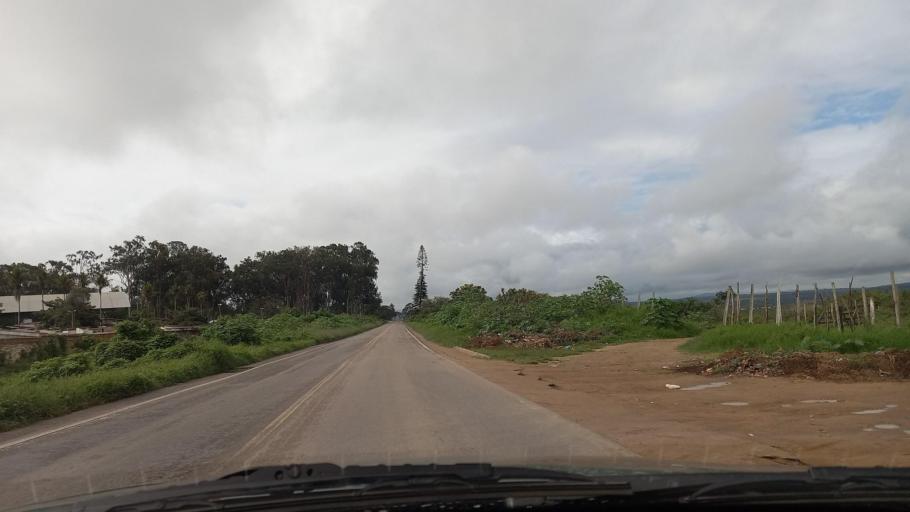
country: BR
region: Pernambuco
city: Garanhuns
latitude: -8.9066
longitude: -36.4980
